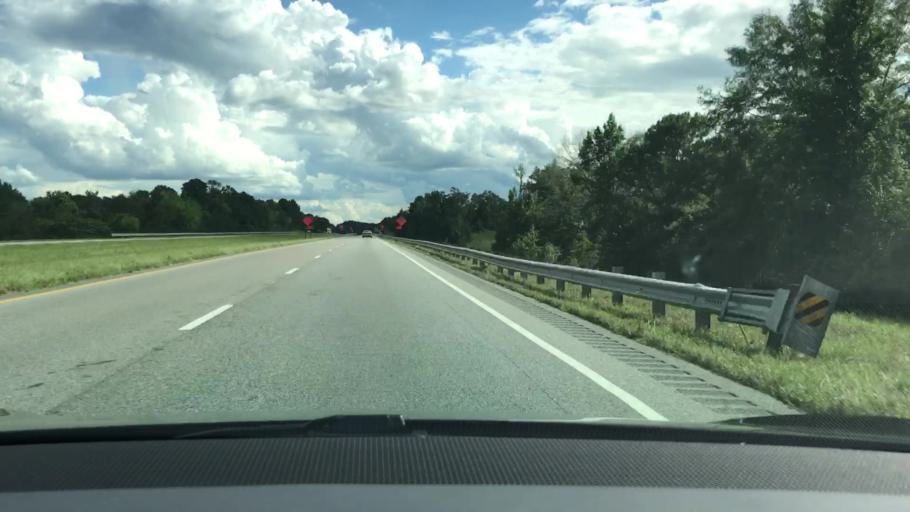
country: US
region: Alabama
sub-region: Pike County
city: Troy
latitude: 31.9851
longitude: -86.0270
